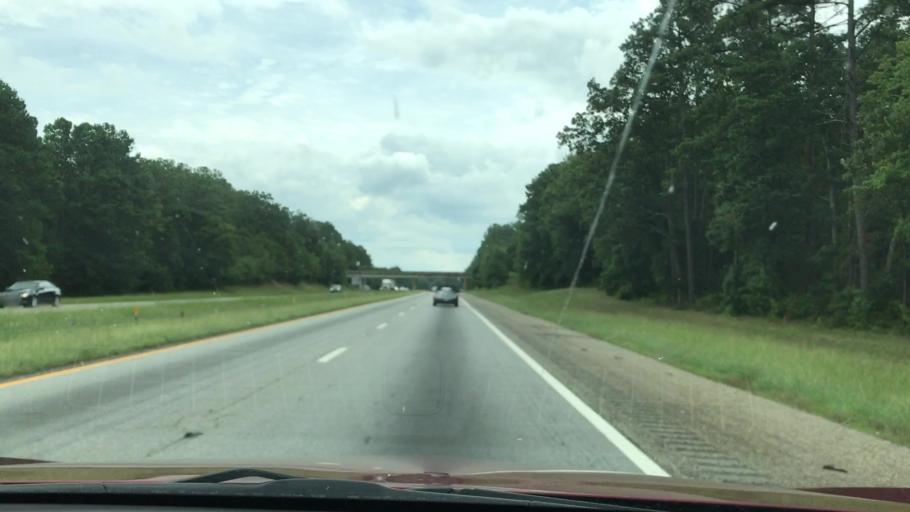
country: US
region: South Carolina
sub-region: Richland County
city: Lake Murray of Richland
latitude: 34.1377
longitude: -81.2200
